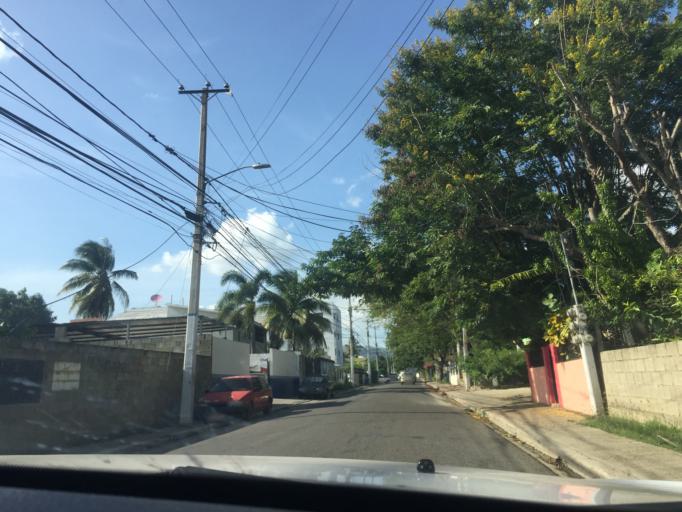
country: DO
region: Santiago
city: Santiago de los Caballeros
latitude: 19.4698
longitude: -70.6581
